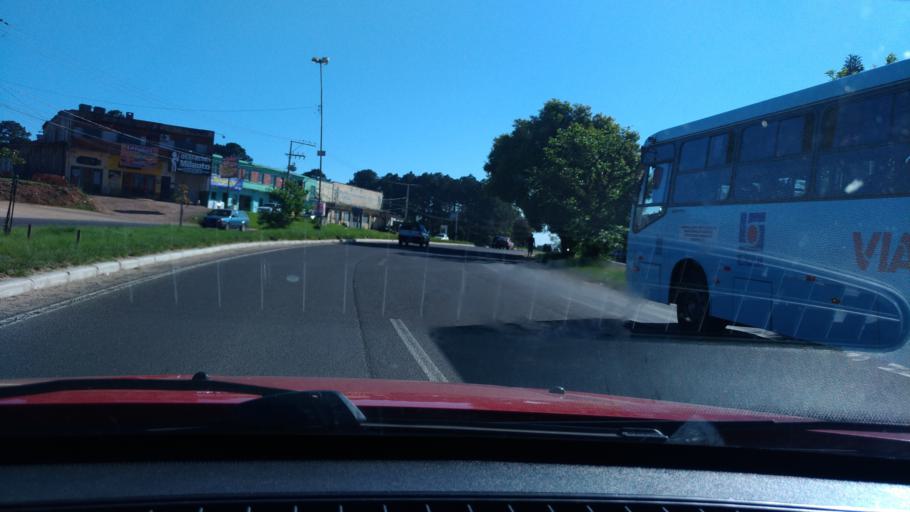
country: BR
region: Rio Grande do Sul
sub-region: Viamao
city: Viamao
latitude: -30.0907
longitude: -51.0628
